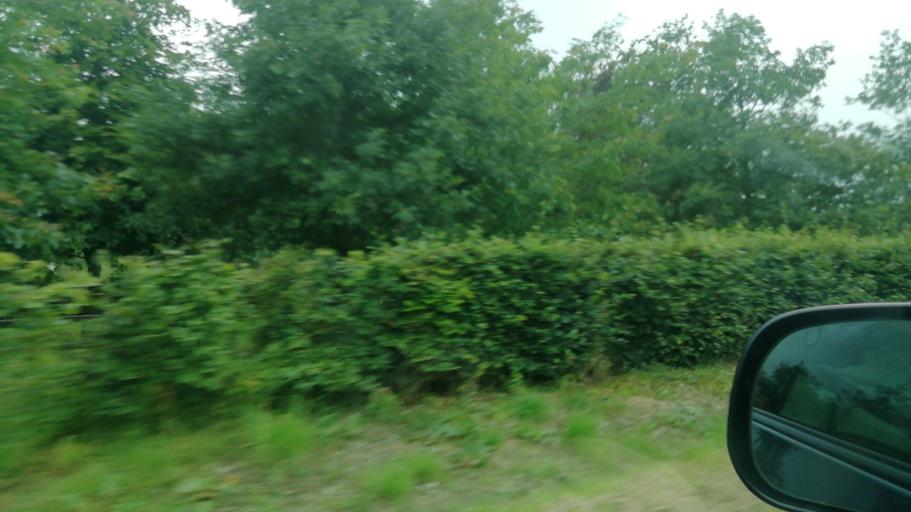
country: IE
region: Munster
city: Fethard
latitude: 52.4919
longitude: -7.6905
